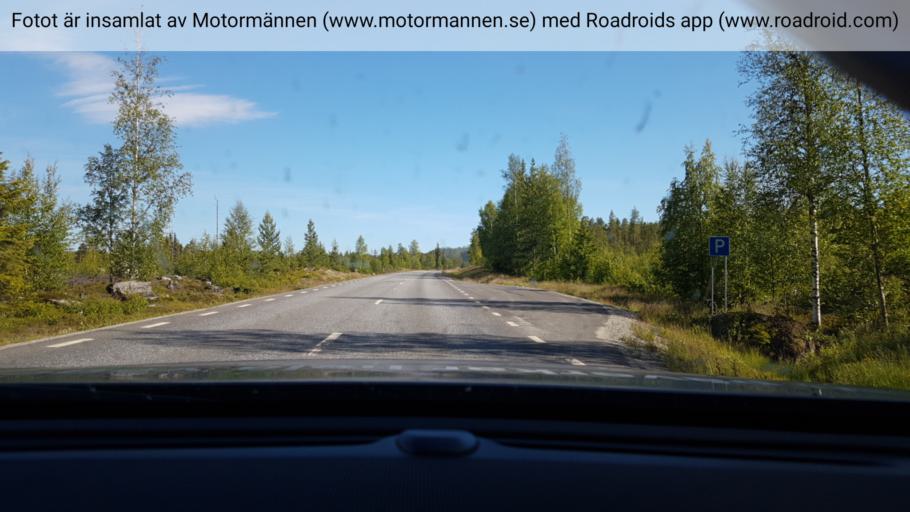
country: SE
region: Vaesterbotten
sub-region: Lycksele Kommun
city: Soderfors
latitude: 64.7387
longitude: 18.2039
